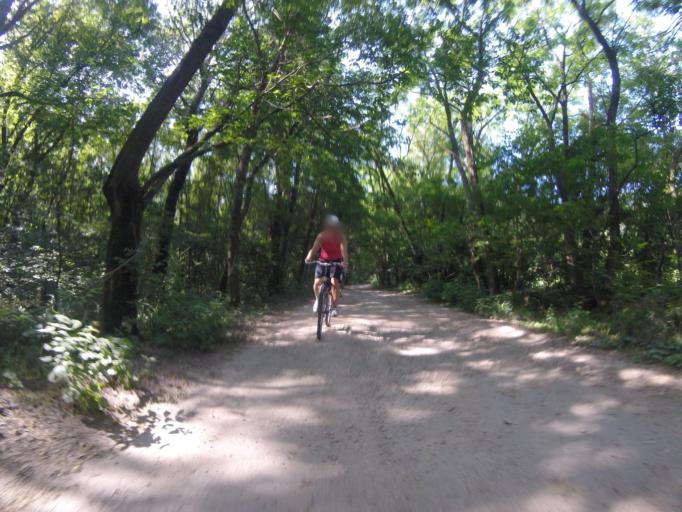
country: HU
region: Tolna
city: Bolcske
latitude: 46.7452
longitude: 18.9741
